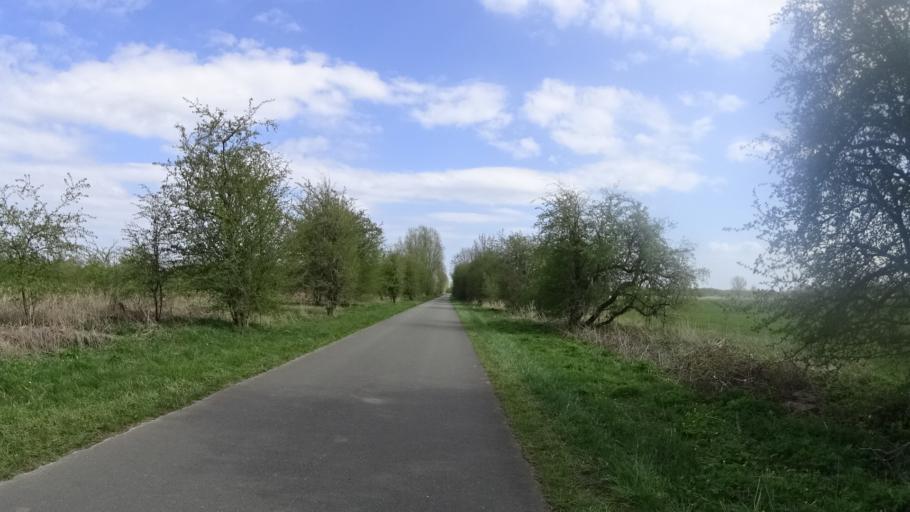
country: DE
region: Lower Saxony
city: Rhede
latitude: 53.0572
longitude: 7.2955
